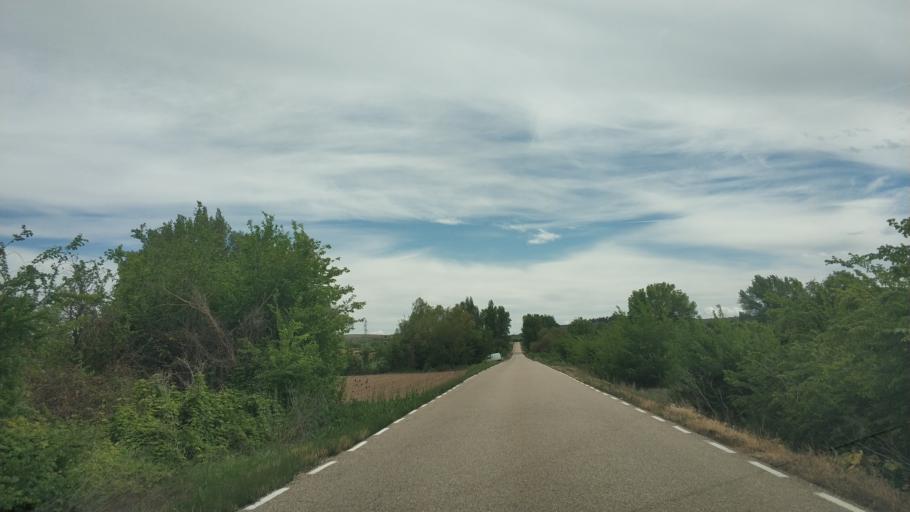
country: ES
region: Castille and Leon
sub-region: Provincia de Soria
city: Berlanga de Duero
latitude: 41.4929
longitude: -2.8683
